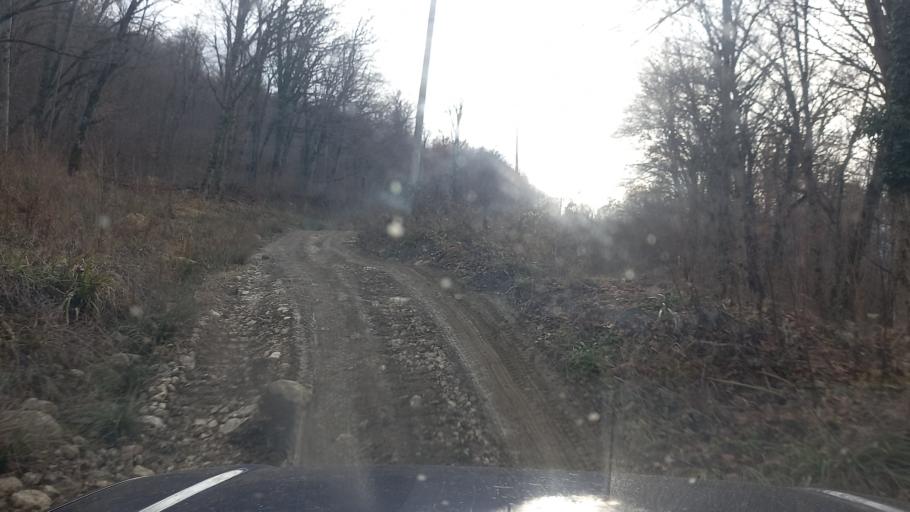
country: RU
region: Krasnodarskiy
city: Neftegorsk
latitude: 44.2110
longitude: 39.7110
